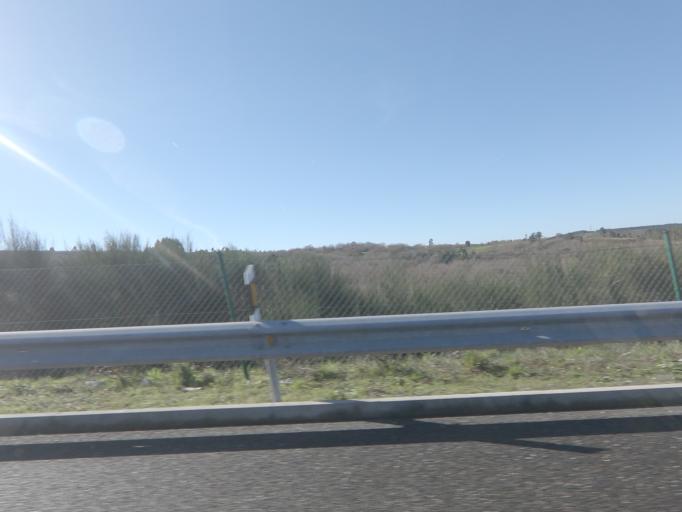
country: ES
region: Galicia
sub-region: Provincia de Pontevedra
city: Dozon
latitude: 42.5673
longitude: -8.0543
